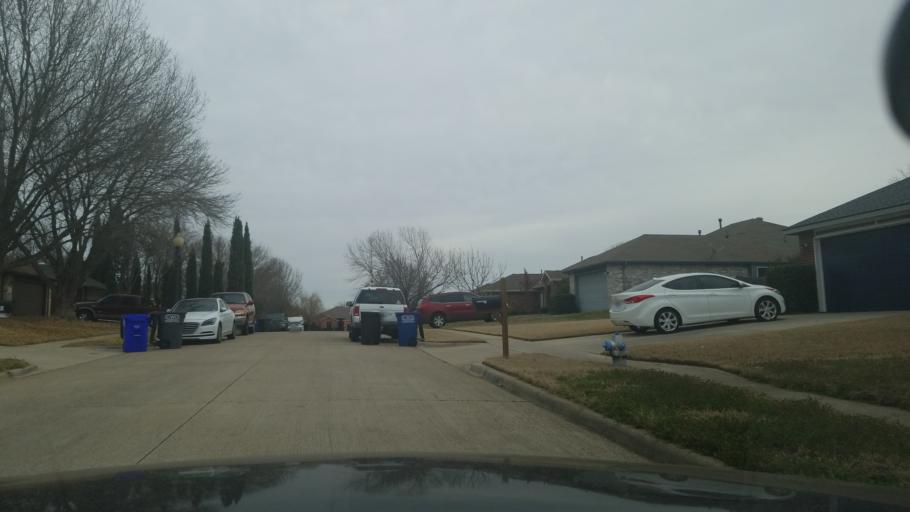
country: US
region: Texas
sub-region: Denton County
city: Hickory Creek
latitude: 33.1319
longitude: -97.0589
